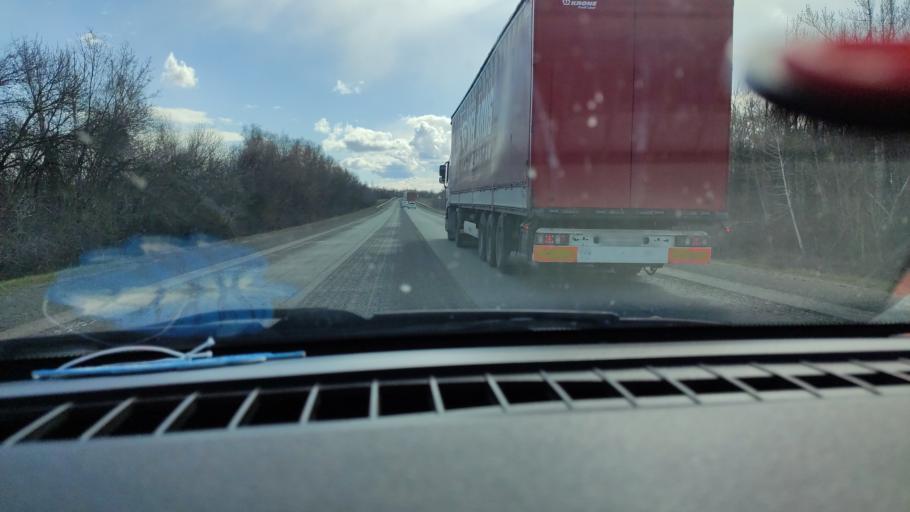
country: RU
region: Saratov
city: Dukhovnitskoye
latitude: 52.6258
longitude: 48.1796
